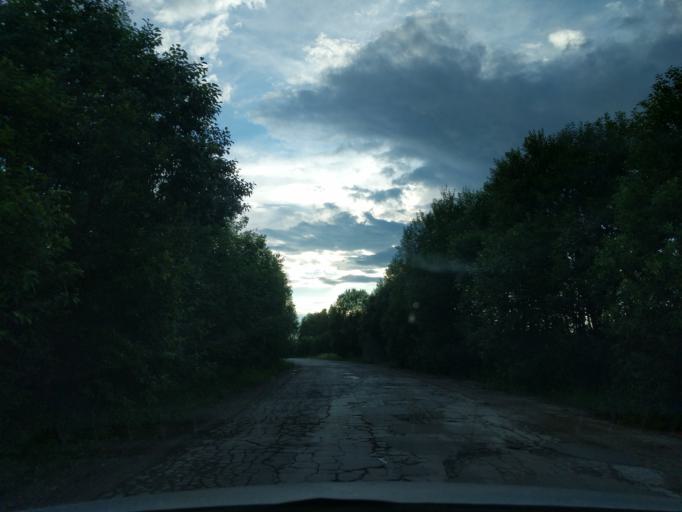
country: RU
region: Kaluga
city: Myatlevo
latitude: 54.8529
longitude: 35.5930
